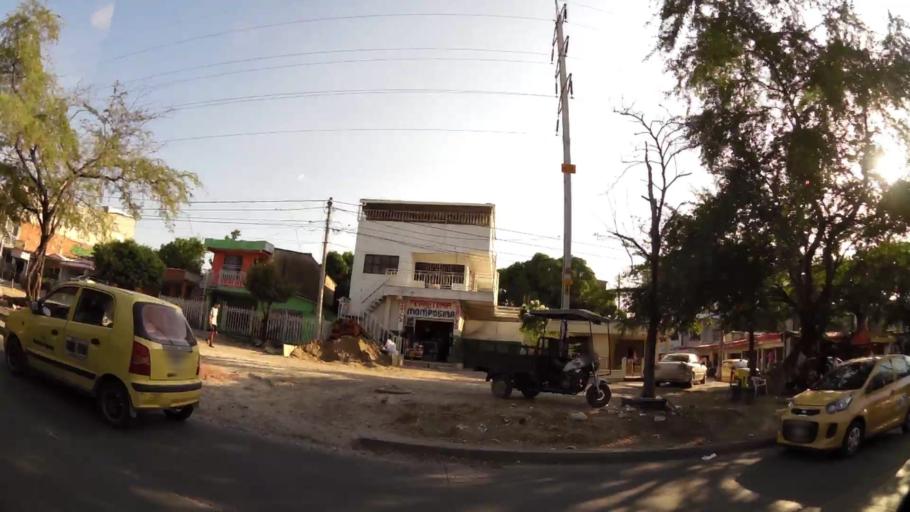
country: CO
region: Bolivar
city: Cartagena
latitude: 10.3796
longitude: -75.4816
